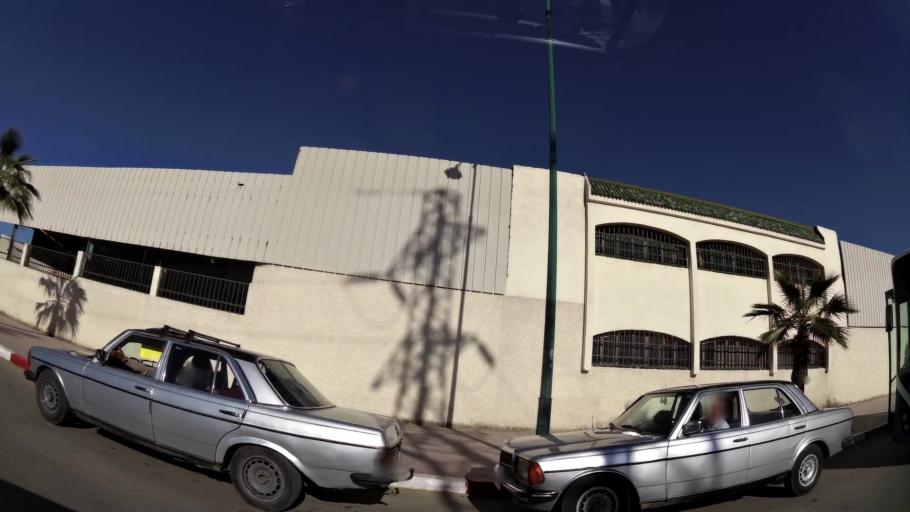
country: MA
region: Meknes-Tafilalet
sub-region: Meknes
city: Meknes
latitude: 33.8734
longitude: -5.5751
